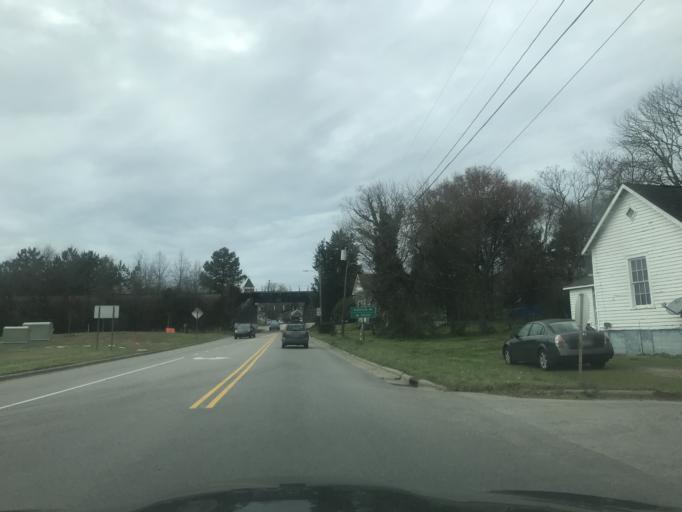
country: US
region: North Carolina
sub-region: Franklin County
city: Franklinton
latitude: 36.1010
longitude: -78.4560
